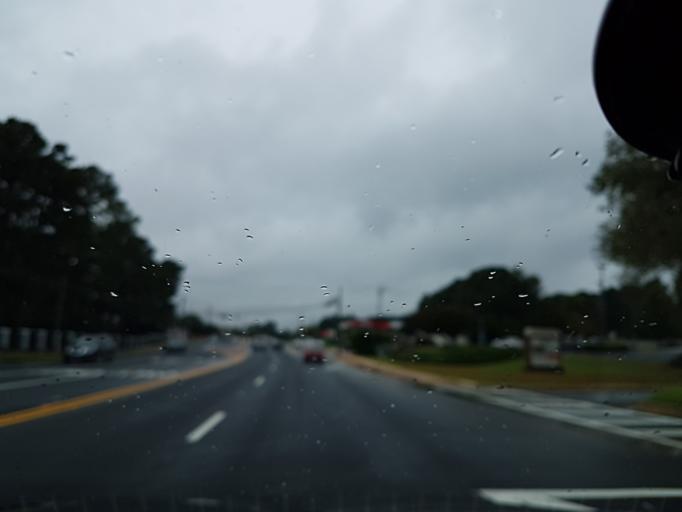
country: US
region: Georgia
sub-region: Gwinnett County
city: Norcross
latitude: 33.9517
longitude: -84.2418
